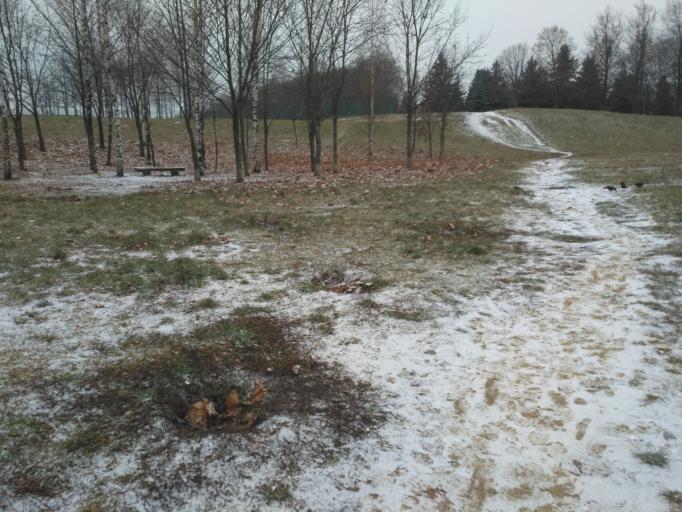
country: BY
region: Minsk
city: Novoye Medvezhino
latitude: 53.9178
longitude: 27.4848
